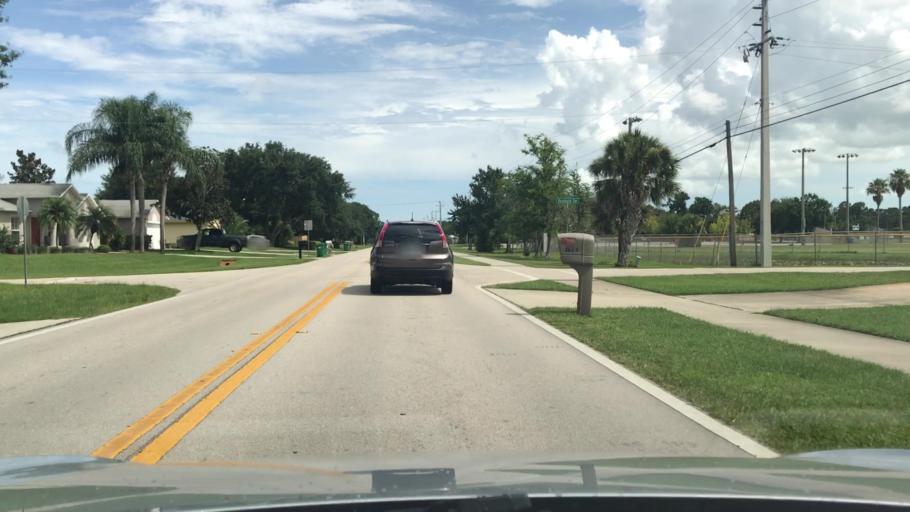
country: US
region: Florida
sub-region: Indian River County
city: Sebastian
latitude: 27.7802
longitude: -80.4880
